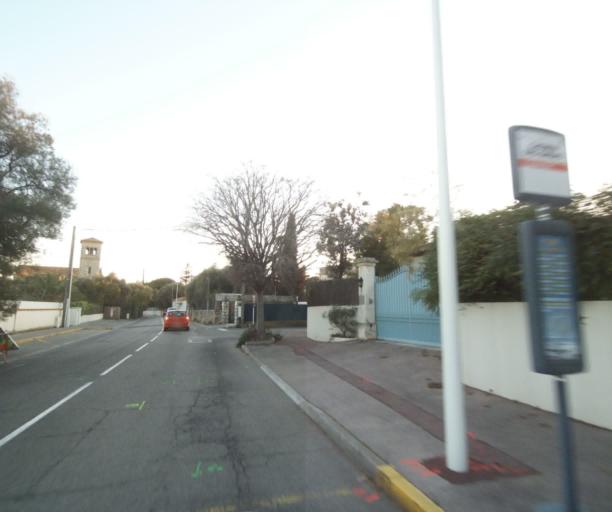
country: FR
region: Provence-Alpes-Cote d'Azur
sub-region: Departement des Alpes-Maritimes
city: Antibes
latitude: 43.5553
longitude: 7.1286
